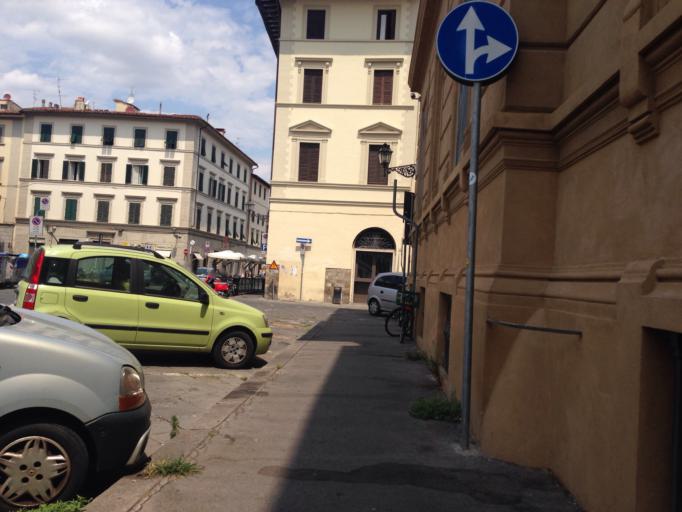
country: IT
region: Tuscany
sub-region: Province of Florence
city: Florence
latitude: 43.7696
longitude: 11.2417
